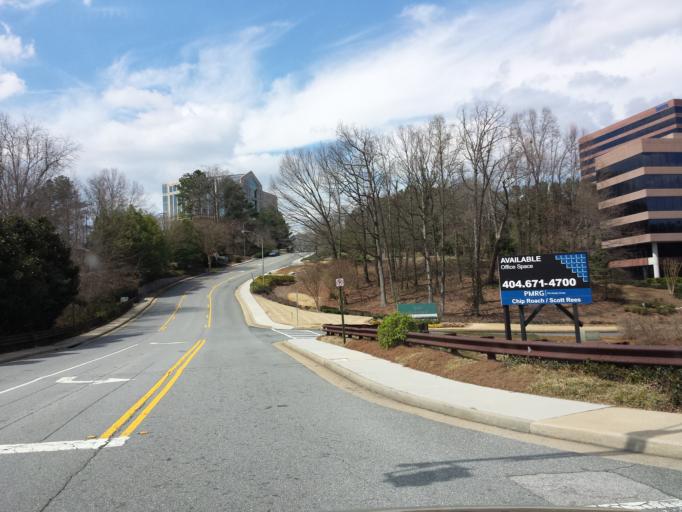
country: US
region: Georgia
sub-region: Cobb County
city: Vinings
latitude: 33.8996
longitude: -84.4587
